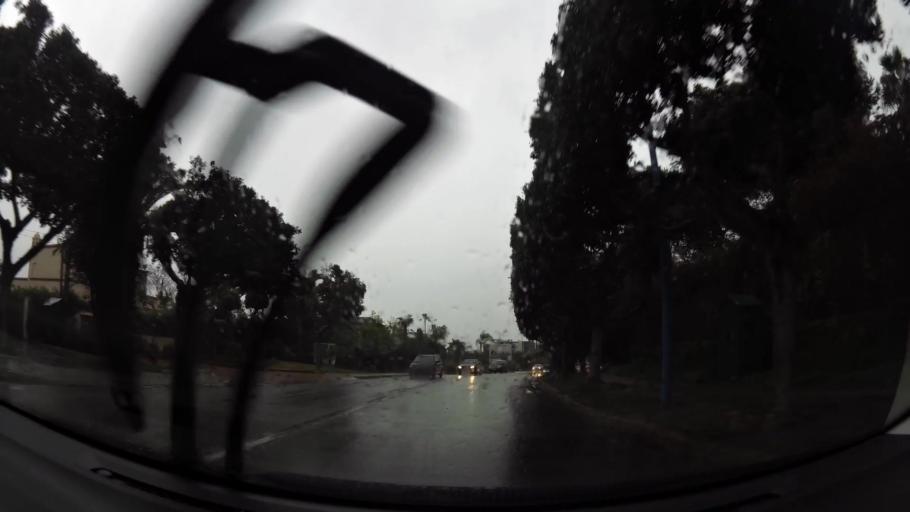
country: MA
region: Grand Casablanca
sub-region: Casablanca
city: Casablanca
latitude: 33.5863
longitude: -7.6677
